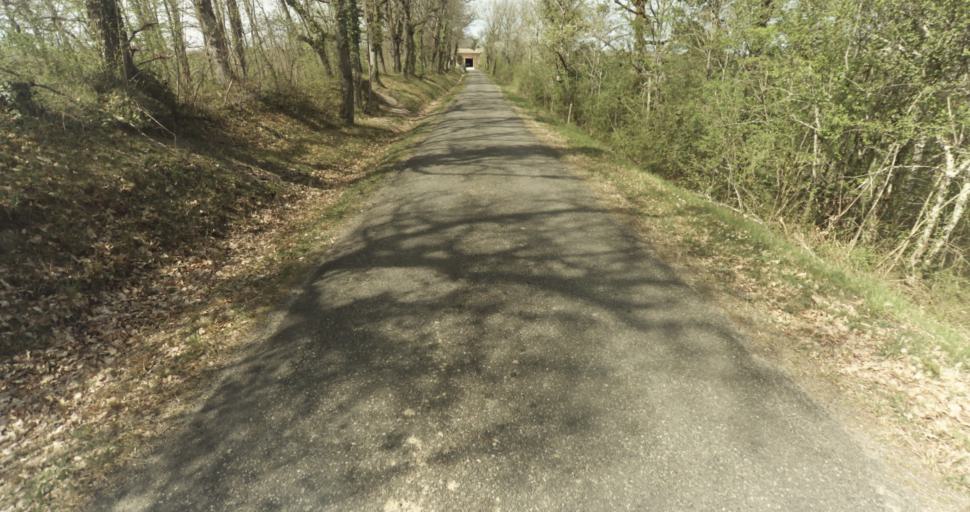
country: FR
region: Midi-Pyrenees
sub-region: Departement du Tarn-et-Garonne
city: Moissac
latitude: 44.1618
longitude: 1.1213
